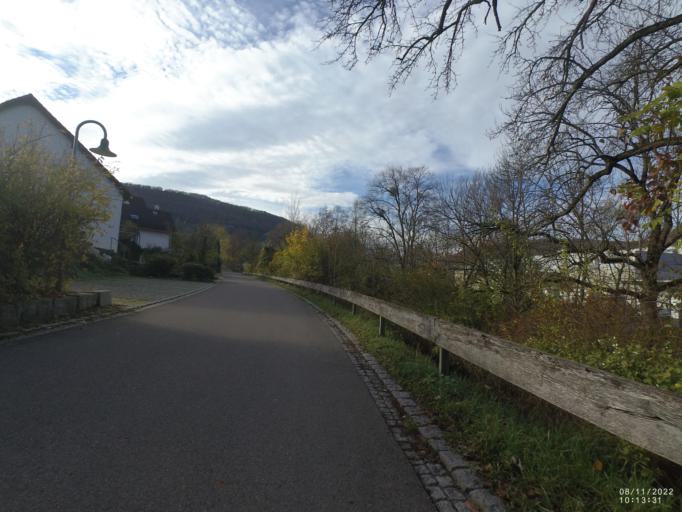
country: DE
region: Baden-Wuerttemberg
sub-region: Regierungsbezirk Stuttgart
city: Deggingen
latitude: 48.6010
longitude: 9.7305
